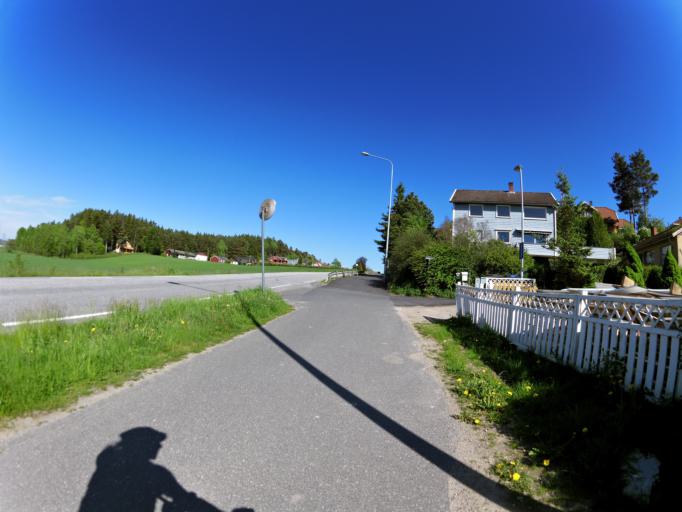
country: NO
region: Ostfold
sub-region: Fredrikstad
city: Fredrikstad
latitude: 59.2304
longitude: 11.0157
